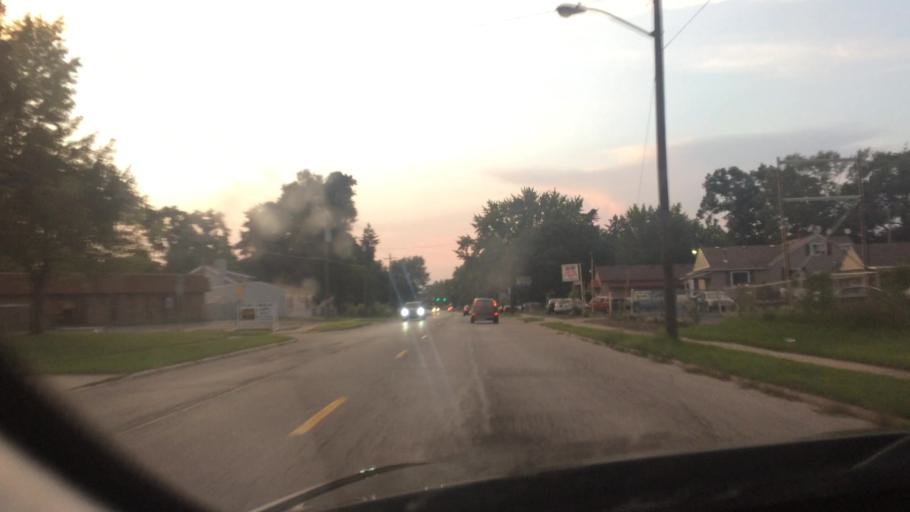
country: US
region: Michigan
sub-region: Monroe County
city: Lambertville
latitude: 41.7123
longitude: -83.6112
